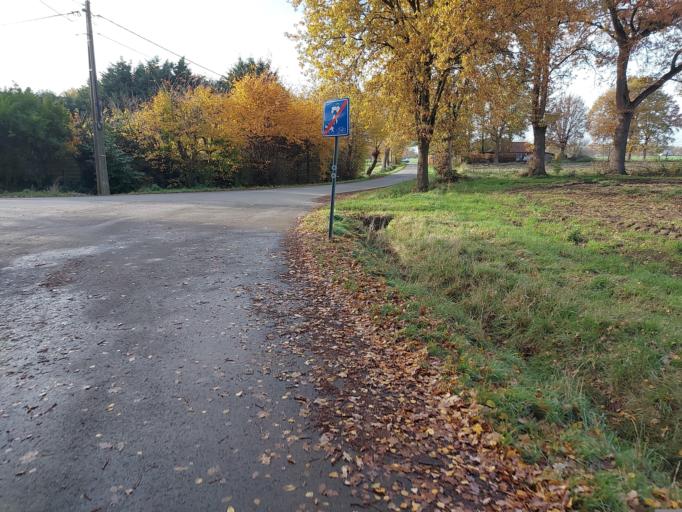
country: BE
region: Flanders
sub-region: Provincie Antwerpen
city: Geel
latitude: 51.1530
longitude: 4.9658
